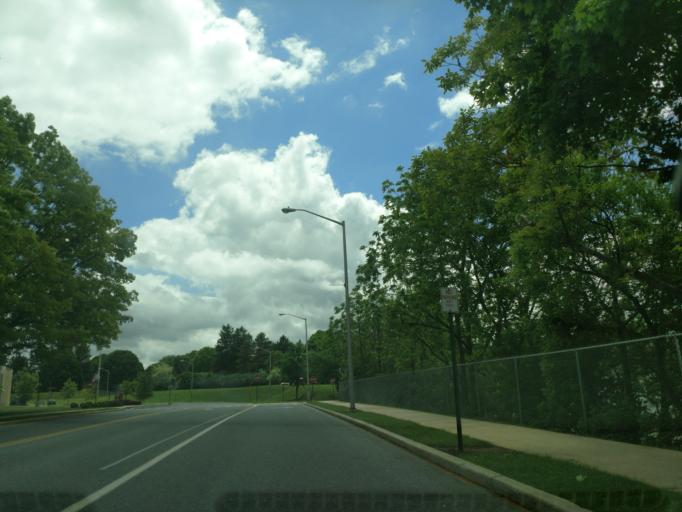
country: US
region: Pennsylvania
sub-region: Lebanon County
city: Lebanon South
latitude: 40.3265
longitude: -76.4225
